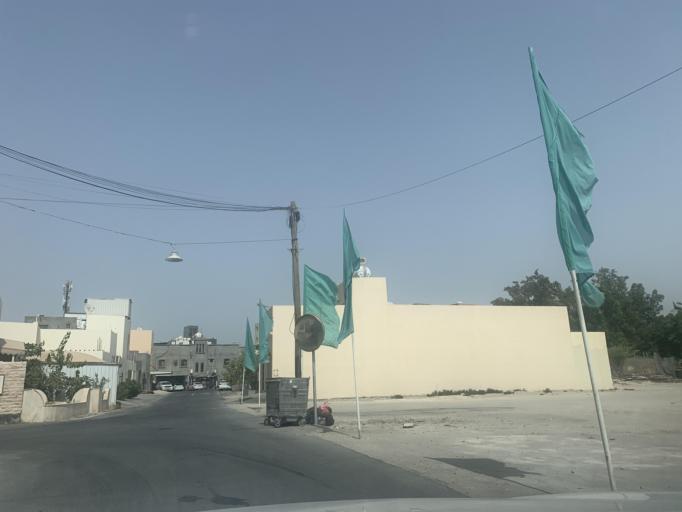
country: BH
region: Manama
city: Jidd Hafs
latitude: 26.2176
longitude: 50.4689
